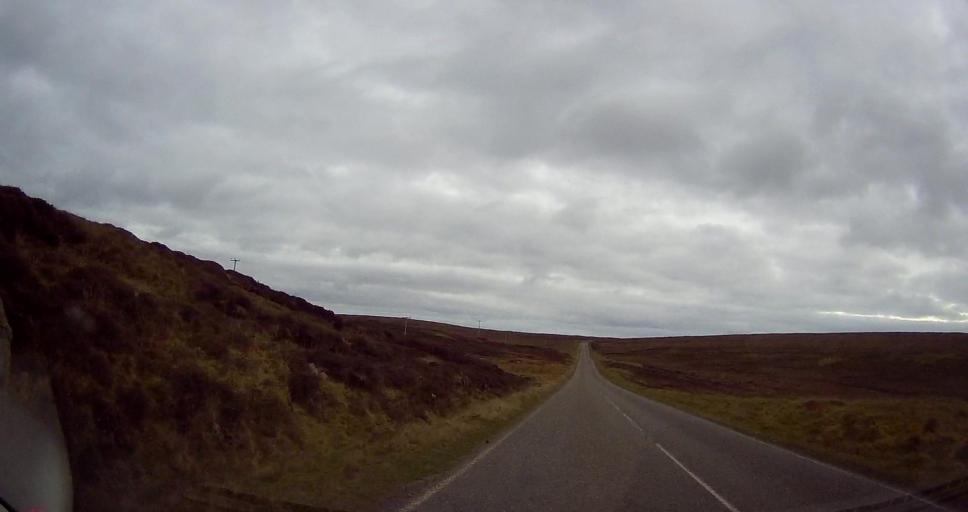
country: GB
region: Scotland
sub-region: Shetland Islands
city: Shetland
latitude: 60.6687
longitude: -1.0120
